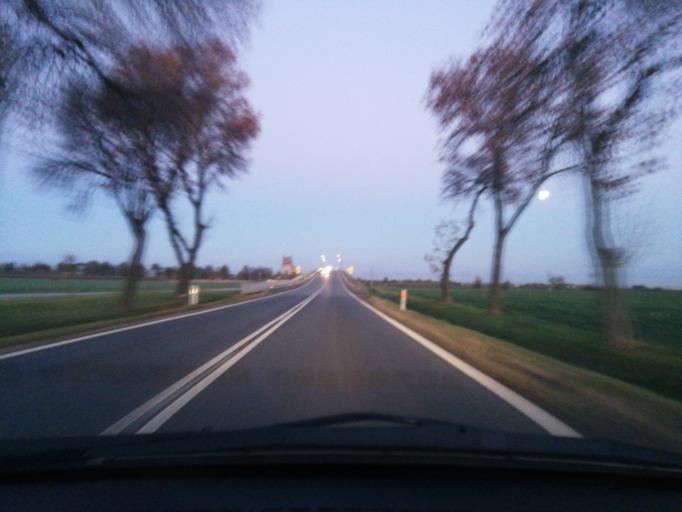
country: PL
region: Lodz Voivodeship
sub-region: Powiat brzezinski
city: Rogow
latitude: 51.8069
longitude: 19.8651
